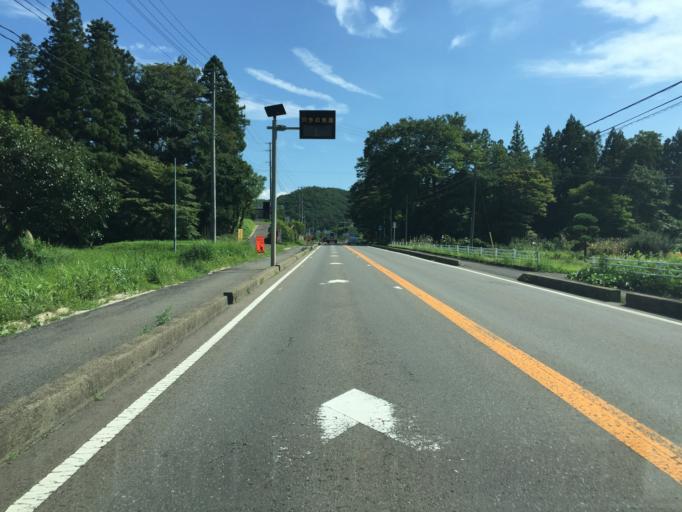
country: JP
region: Fukushima
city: Fukushima-shi
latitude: 37.7126
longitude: 140.5028
